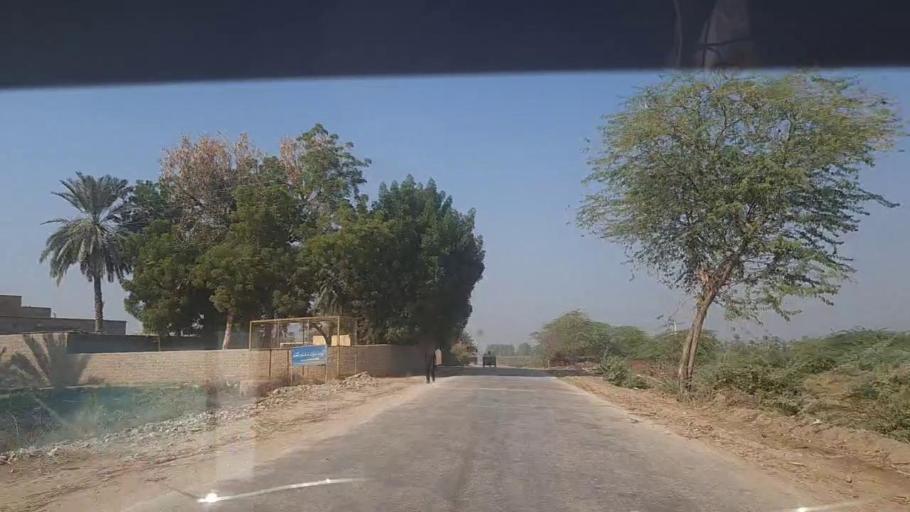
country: PK
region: Sindh
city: Kot Diji
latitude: 27.4189
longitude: 68.6622
